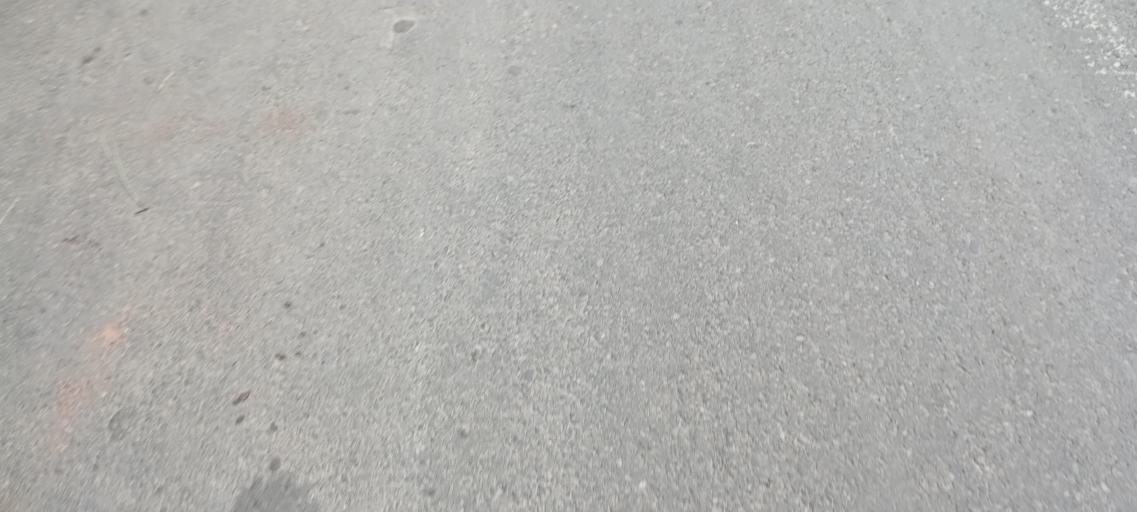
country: NP
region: Central Region
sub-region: Bagmati Zone
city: Kathmandu
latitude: 27.7797
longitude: 85.3634
